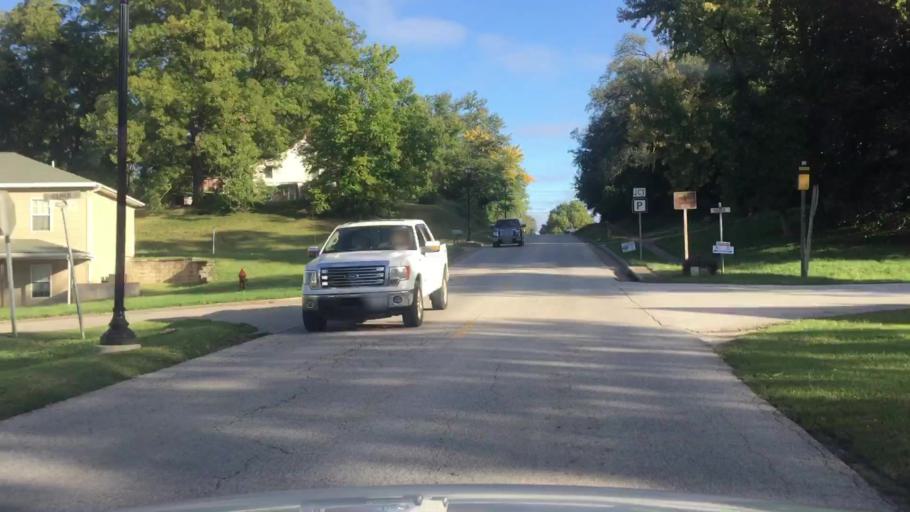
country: US
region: Missouri
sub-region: Howard County
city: New Franklin
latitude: 39.0151
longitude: -92.7375
